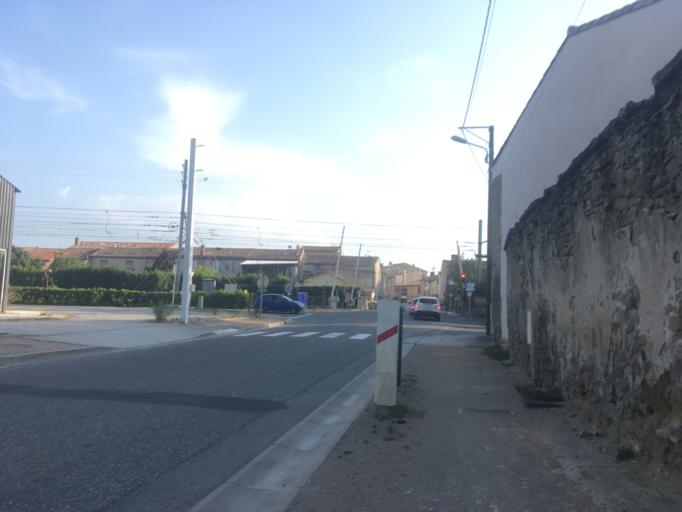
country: FR
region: Languedoc-Roussillon
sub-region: Departement de l'Aude
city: Bram
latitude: 43.2452
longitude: 2.1158
